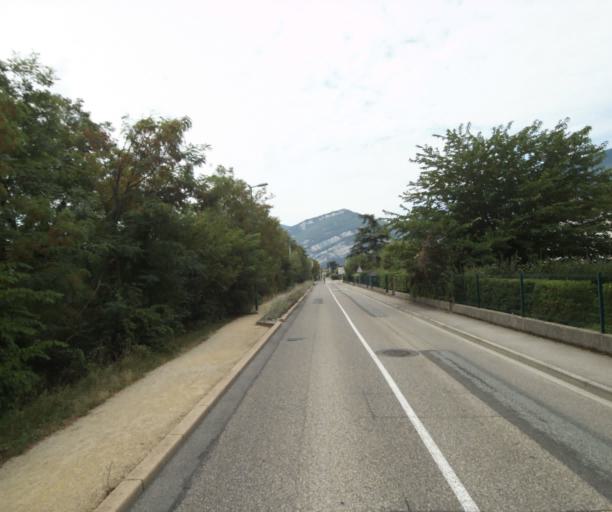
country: FR
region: Rhone-Alpes
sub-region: Departement de l'Isere
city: Saint-Egreve
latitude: 45.2341
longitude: 5.6869
